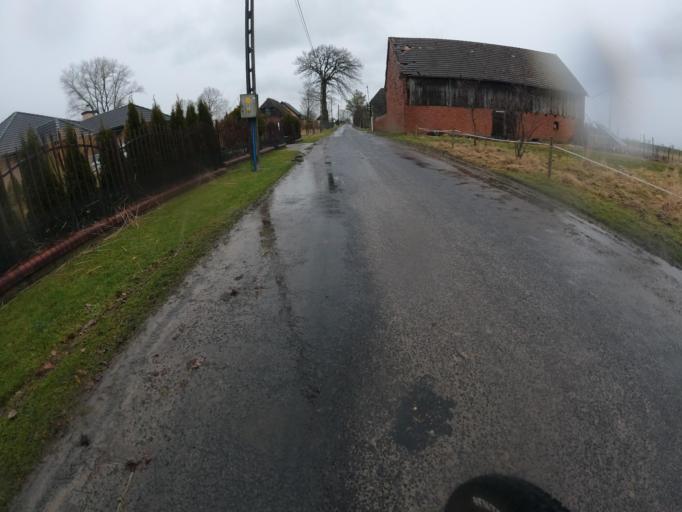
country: PL
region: West Pomeranian Voivodeship
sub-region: Powiat slawienski
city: Darlowo
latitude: 54.3969
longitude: 16.5302
